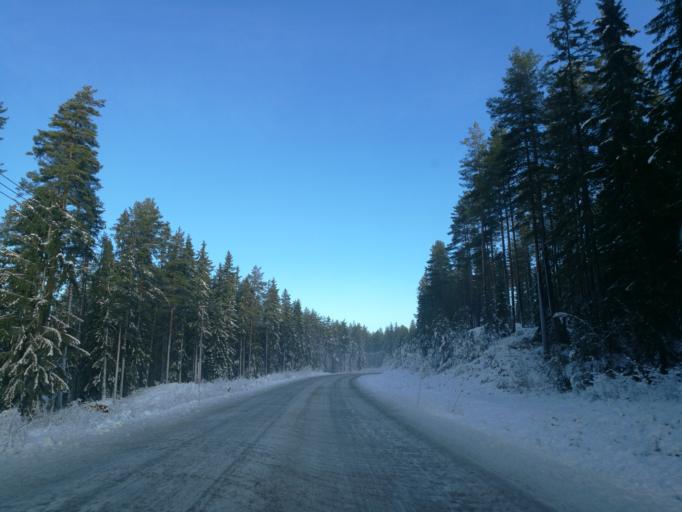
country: NO
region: Hedmark
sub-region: Grue
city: Kirkenaer
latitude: 60.3831
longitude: 12.3589
